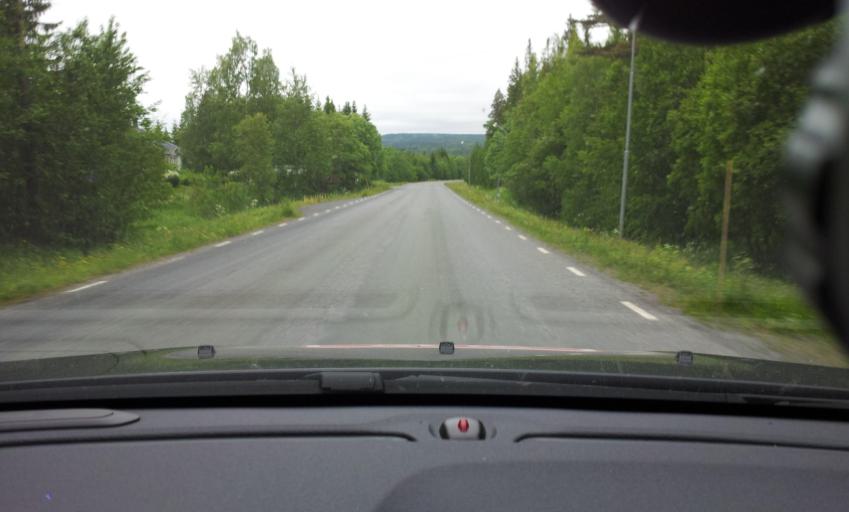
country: SE
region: Jaemtland
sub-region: Are Kommun
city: Jarpen
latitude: 63.2940
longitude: 13.7136
